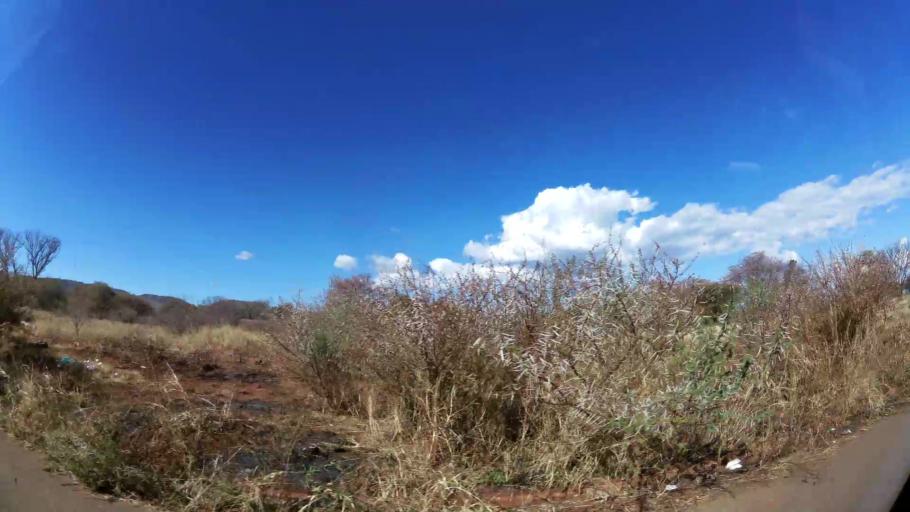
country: ZA
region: Limpopo
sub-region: Waterberg District Municipality
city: Mokopane
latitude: -24.1927
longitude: 29.0163
